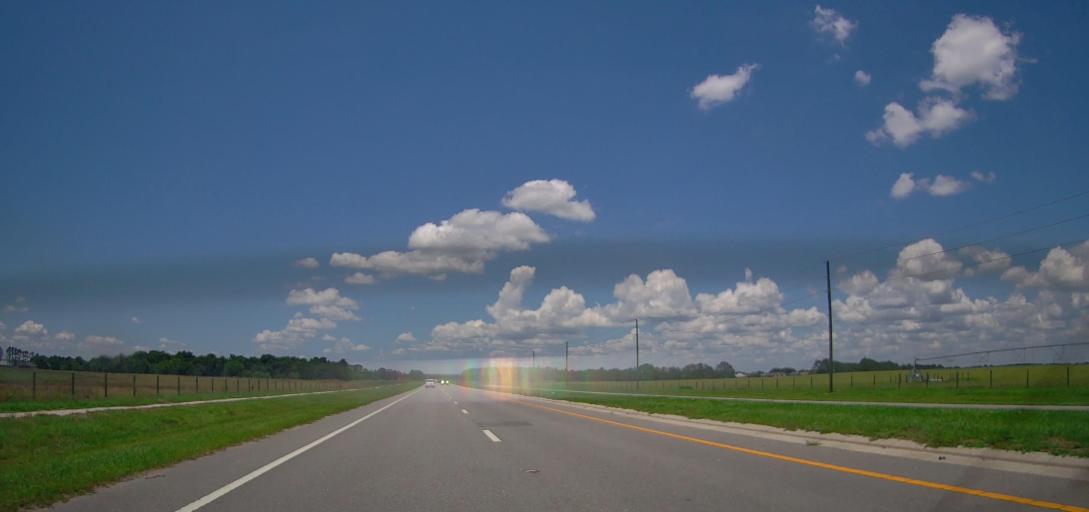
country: US
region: Florida
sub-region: Marion County
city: Silver Springs Shores
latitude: 29.0742
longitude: -82.0300
